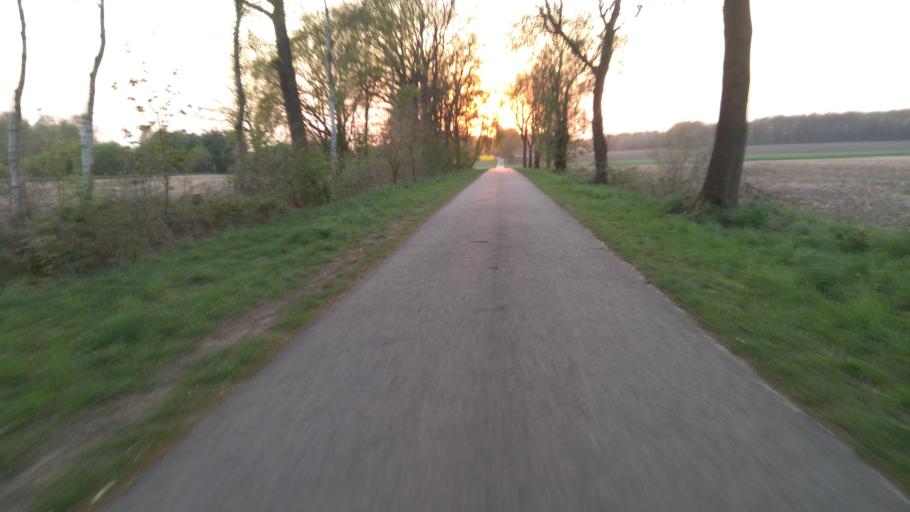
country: DE
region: Lower Saxony
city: Harsefeld
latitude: 53.4926
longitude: 9.5116
